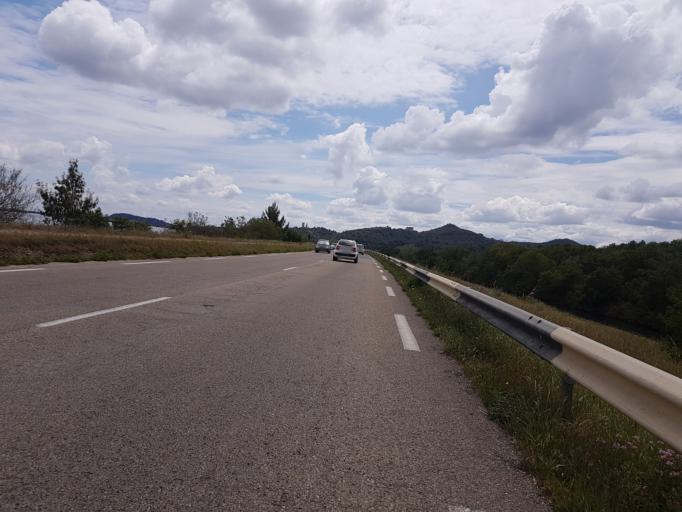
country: FR
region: Languedoc-Roussillon
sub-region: Departement du Gard
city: Vallabregues
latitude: 43.8580
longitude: 4.6174
